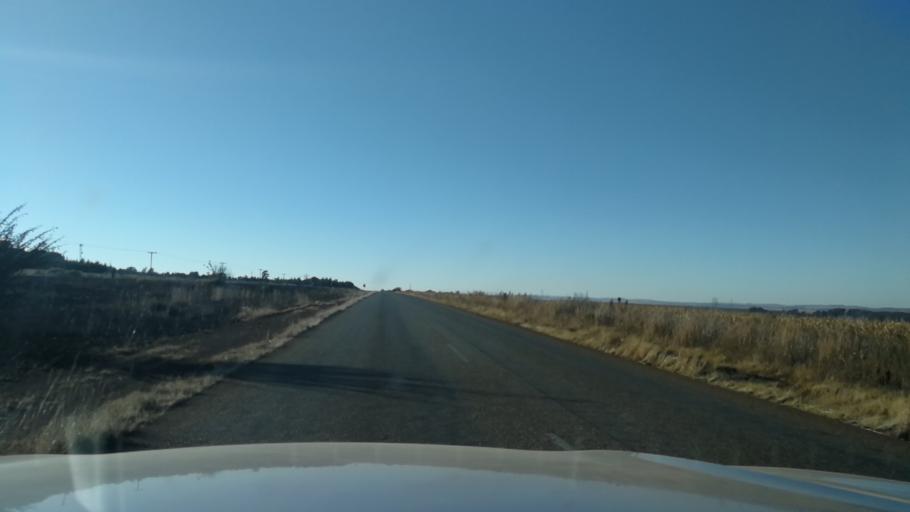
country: ZA
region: North-West
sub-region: Bojanala Platinum District Municipality
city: Koster
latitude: -25.9374
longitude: 27.1505
